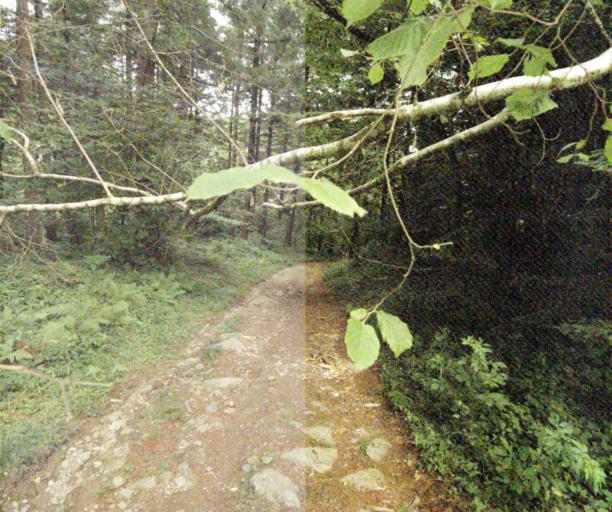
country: FR
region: Midi-Pyrenees
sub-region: Departement du Tarn
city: Soreze
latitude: 43.4193
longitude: 2.1126
